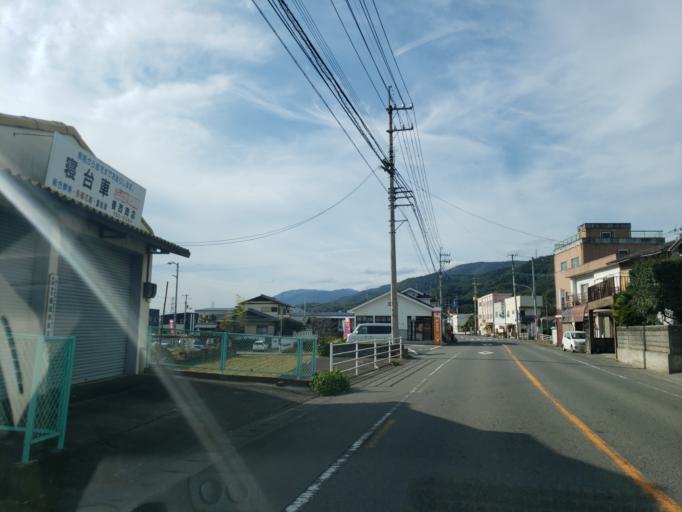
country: JP
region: Tokushima
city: Wakimachi
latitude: 34.0697
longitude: 134.1433
